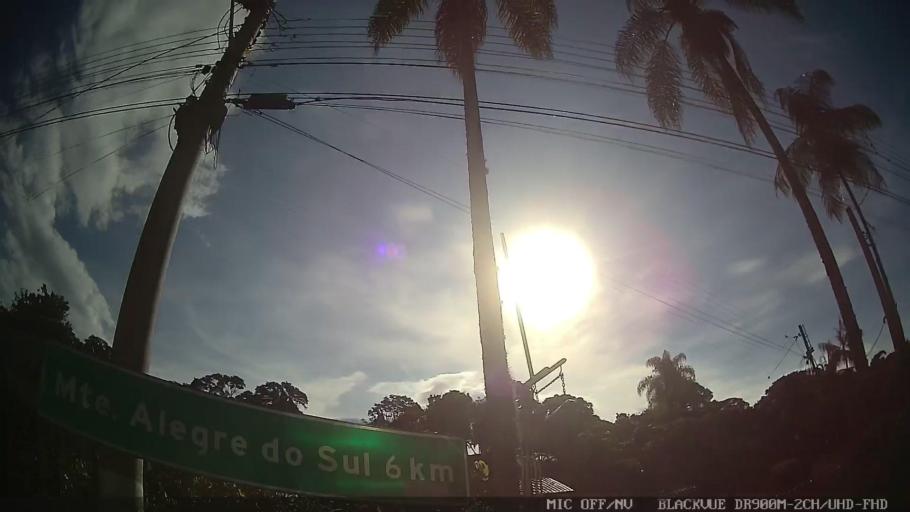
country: BR
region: Sao Paulo
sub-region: Serra Negra
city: Serra Negra
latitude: -22.6356
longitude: -46.6983
